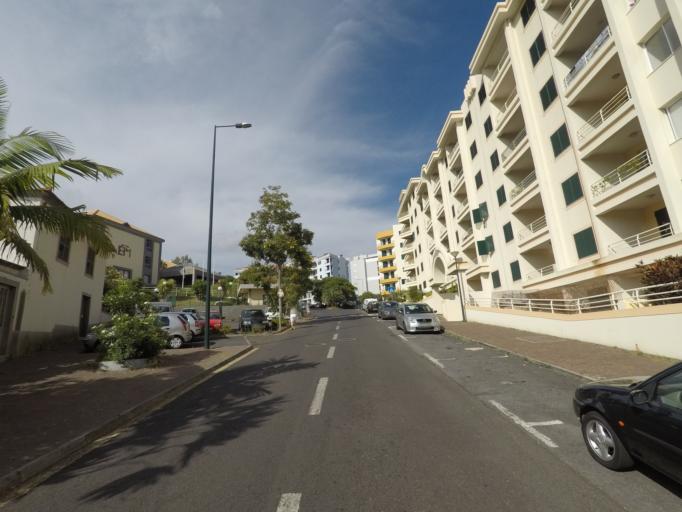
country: PT
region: Madeira
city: Camara de Lobos
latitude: 32.6427
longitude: -16.9484
